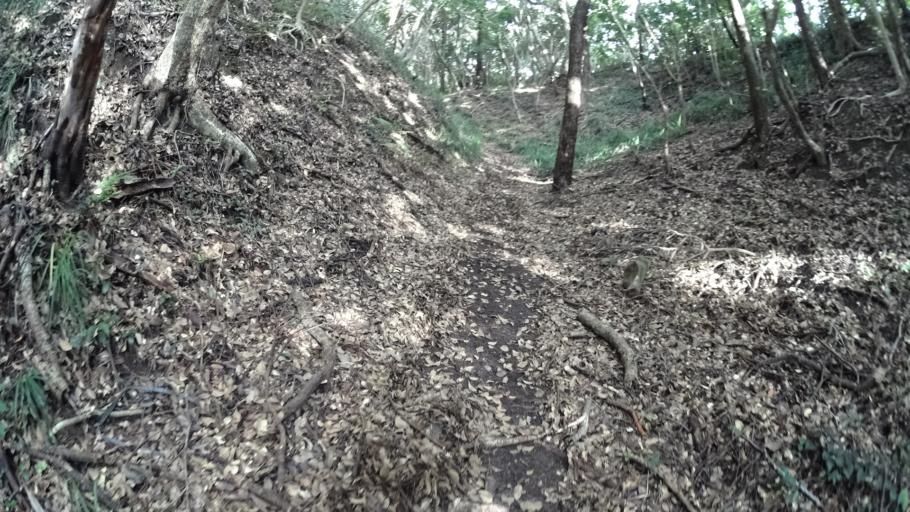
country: JP
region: Shizuoka
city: Shimoda
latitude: 34.3300
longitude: 139.2111
